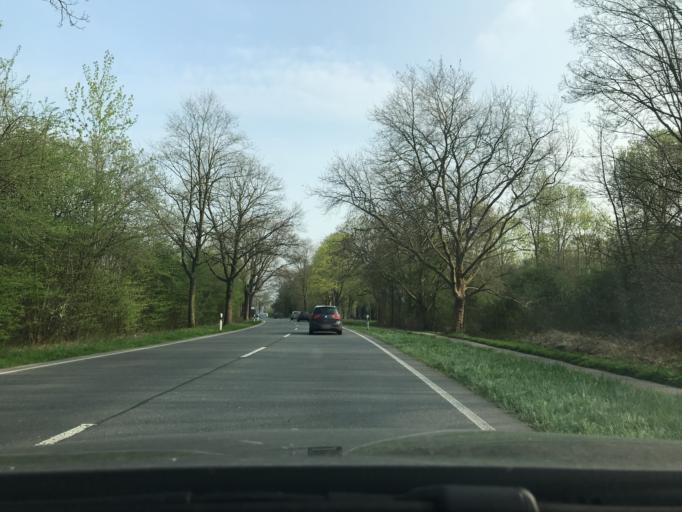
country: DE
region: North Rhine-Westphalia
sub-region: Regierungsbezirk Dusseldorf
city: Kevelaer
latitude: 51.5991
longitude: 6.2320
